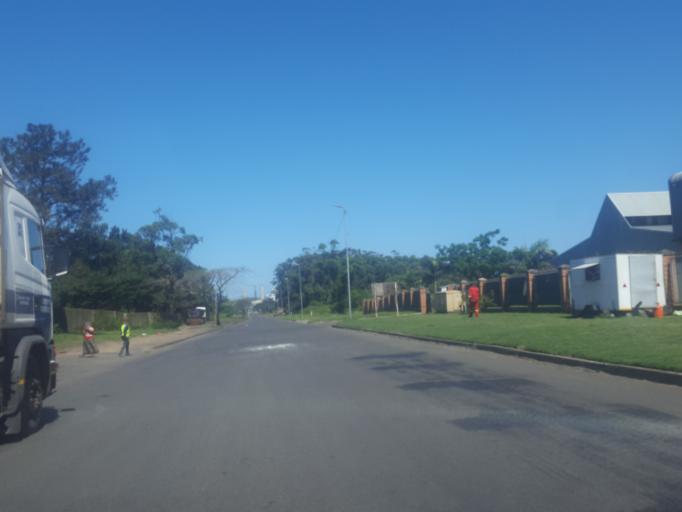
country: ZA
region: KwaZulu-Natal
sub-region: uThungulu District Municipality
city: Richards Bay
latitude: -28.7584
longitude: 32.0163
